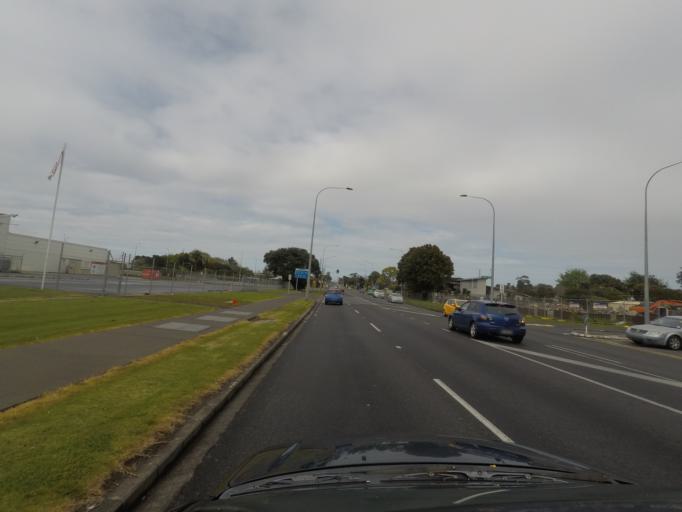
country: NZ
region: Auckland
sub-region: Auckland
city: Tamaki
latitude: -36.9022
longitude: 174.8427
